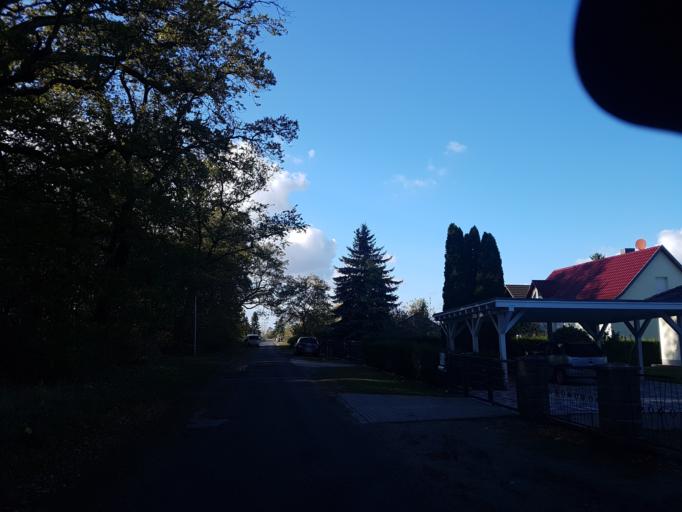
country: DE
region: Brandenburg
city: Nauen
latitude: 52.6356
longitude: 12.9058
